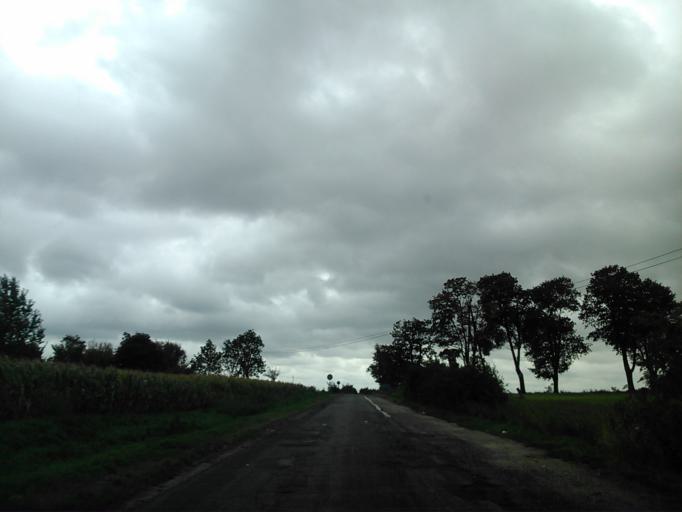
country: PL
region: Kujawsko-Pomorskie
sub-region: Powiat radziejowski
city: Piotrkow Kujawski
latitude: 52.6140
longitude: 18.4164
